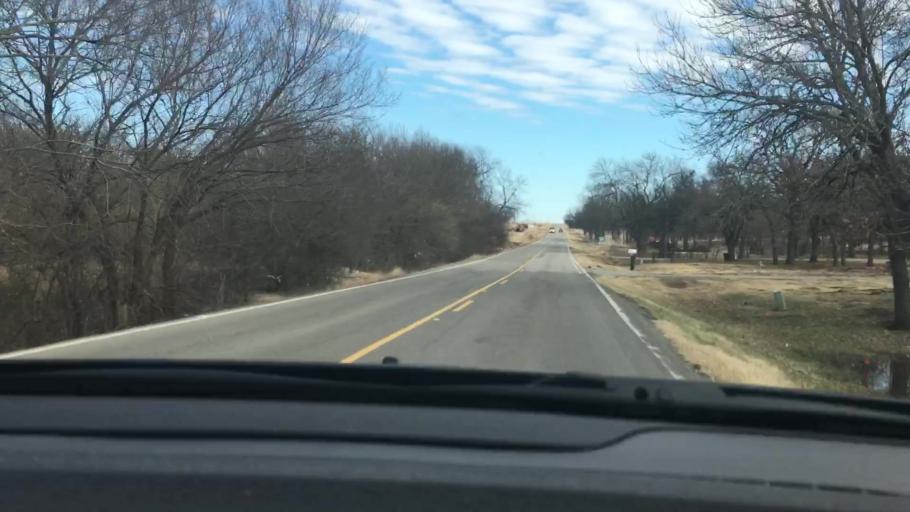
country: US
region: Oklahoma
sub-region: Garvin County
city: Stratford
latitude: 34.7966
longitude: -96.9346
